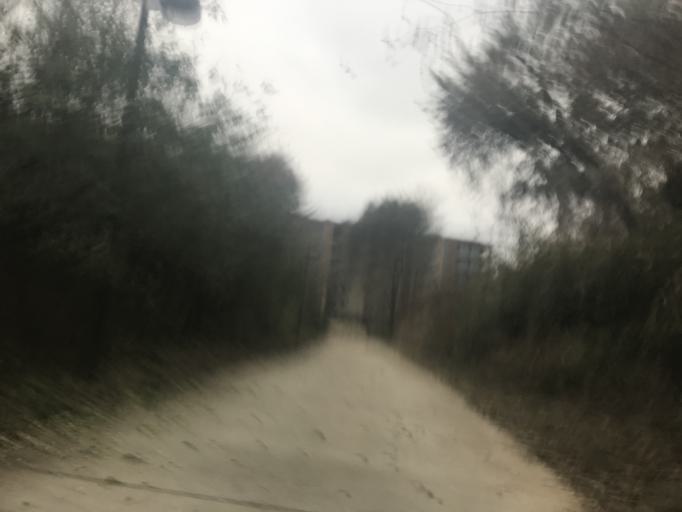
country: US
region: Indiana
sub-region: Clark County
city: Jeffersonville
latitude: 38.2667
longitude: -85.7226
